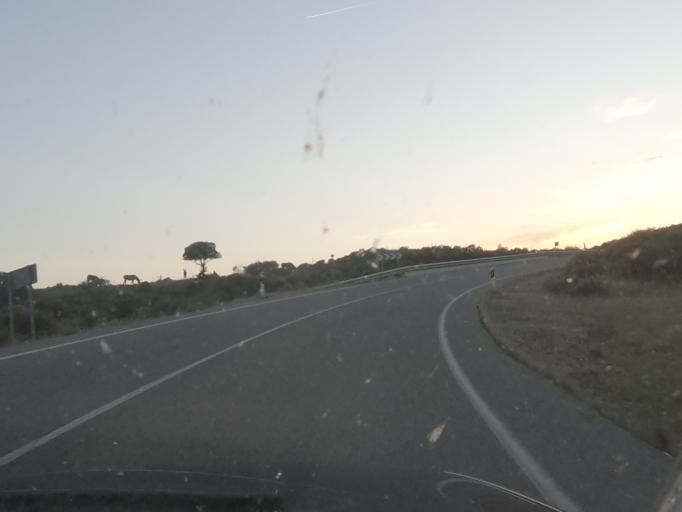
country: ES
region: Extremadura
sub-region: Provincia de Caceres
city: Alcantara
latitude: 39.7305
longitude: -6.9011
